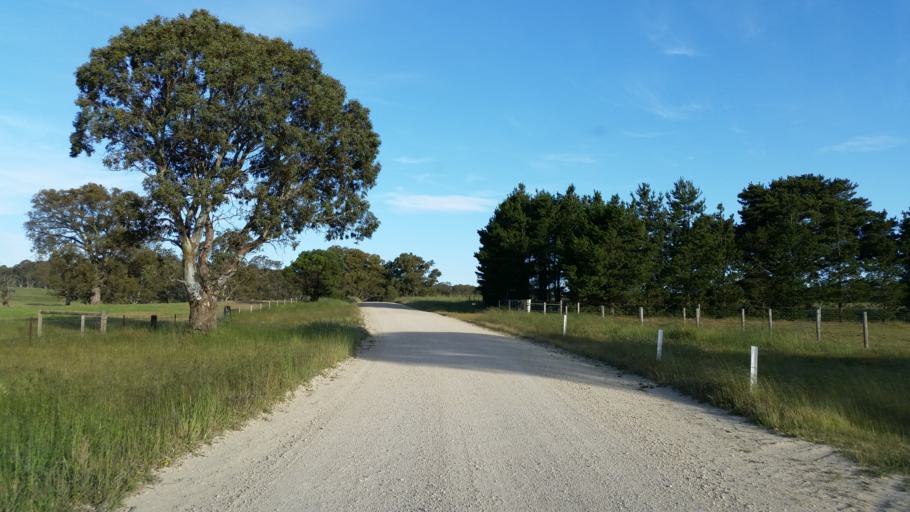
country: AU
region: South Australia
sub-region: Barossa
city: Angaston
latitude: -34.6824
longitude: 139.1113
